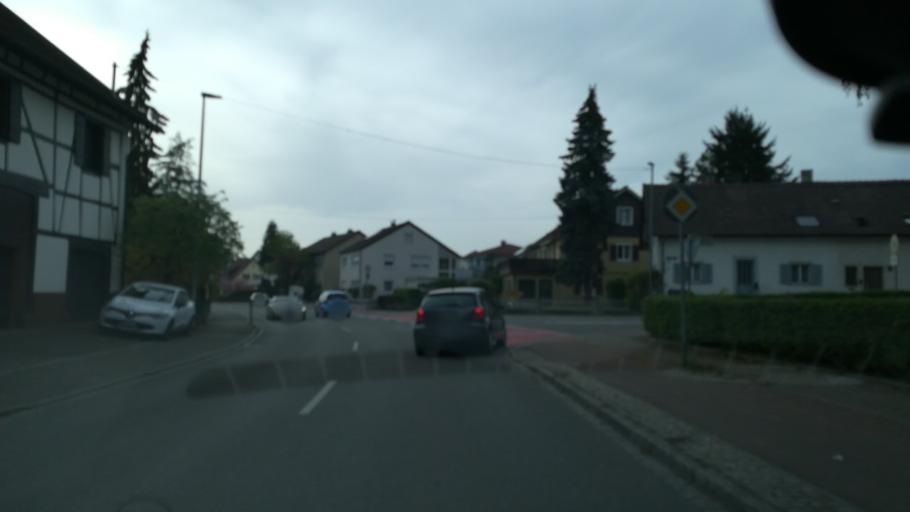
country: DE
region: Baden-Wuerttemberg
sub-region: Freiburg Region
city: Moos
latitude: 47.7537
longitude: 8.9386
